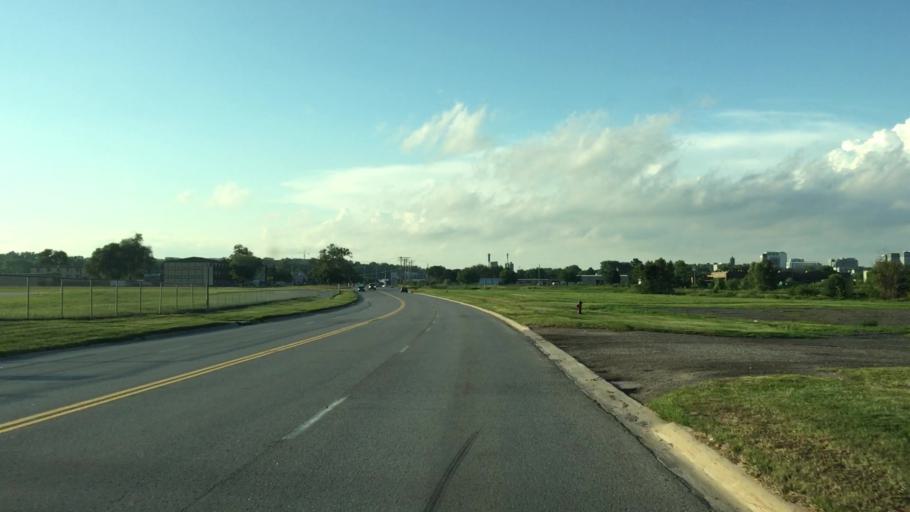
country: US
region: Iowa
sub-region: Johnson County
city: Iowa City
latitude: 41.6418
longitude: -91.5391
